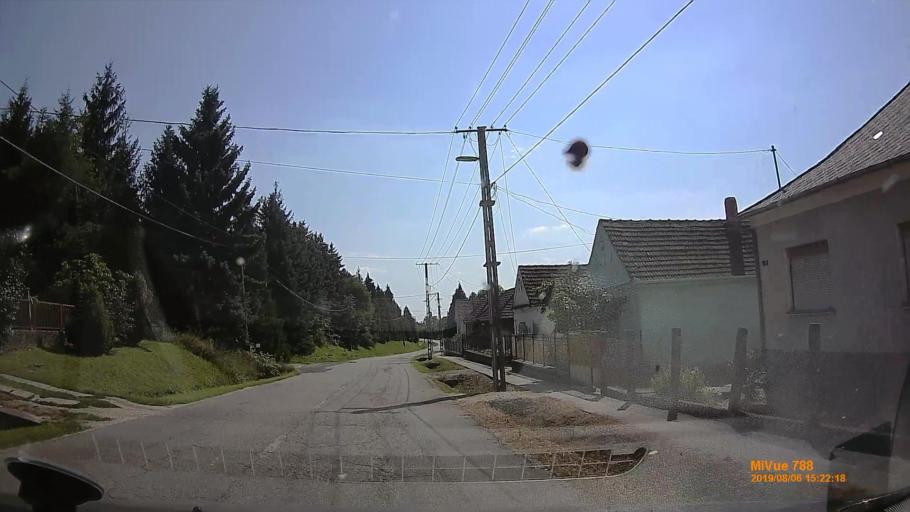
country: HR
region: Koprivnicko-Krizevacka
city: Drnje
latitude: 46.2696
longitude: 16.9475
